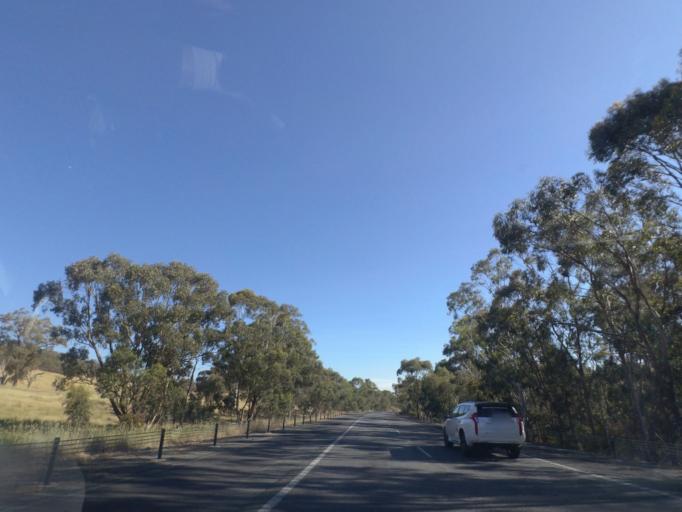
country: AU
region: Victoria
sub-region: Murrindindi
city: Kinglake West
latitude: -37.1657
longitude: 145.0780
